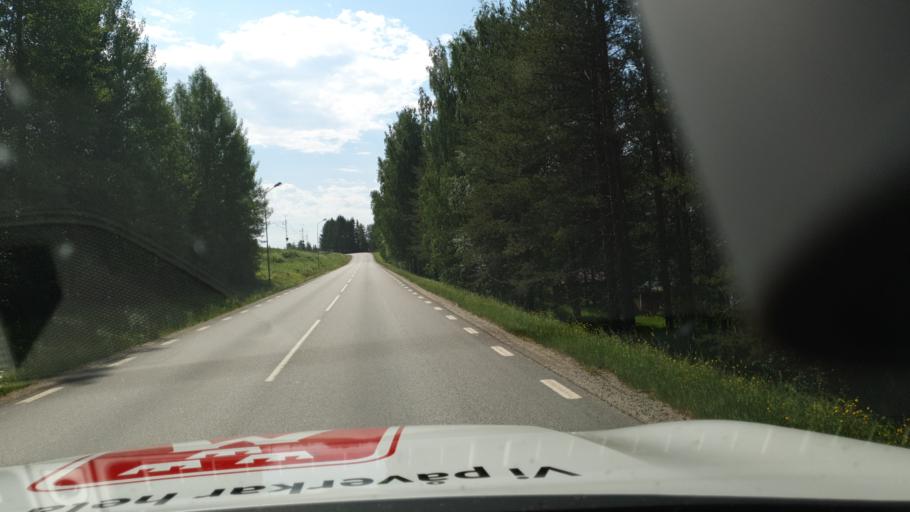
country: SE
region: Vaesterbotten
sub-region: Vindelns Kommun
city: Vindeln
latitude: 64.2242
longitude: 19.7070
